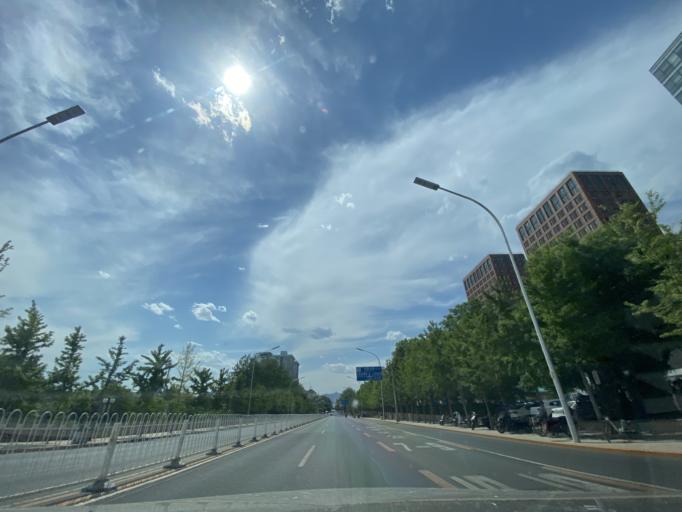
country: CN
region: Beijing
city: Lugu
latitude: 39.9062
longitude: 116.1966
